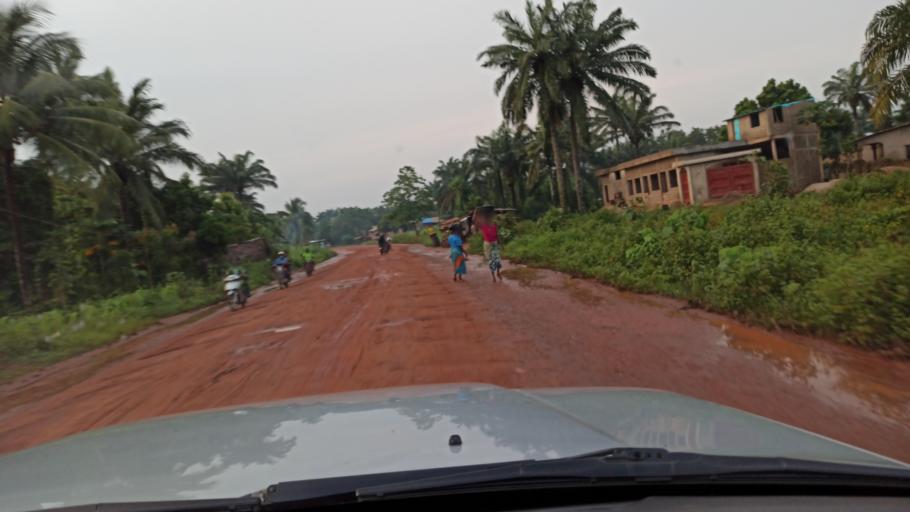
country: BJ
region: Queme
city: Porto-Novo
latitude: 6.5477
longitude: 2.6128
